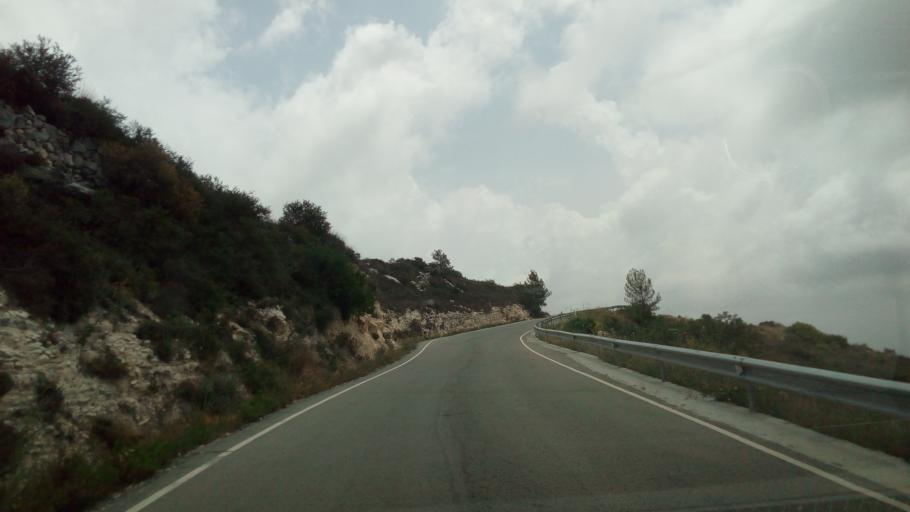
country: CY
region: Limassol
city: Pachna
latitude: 34.8364
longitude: 32.8770
